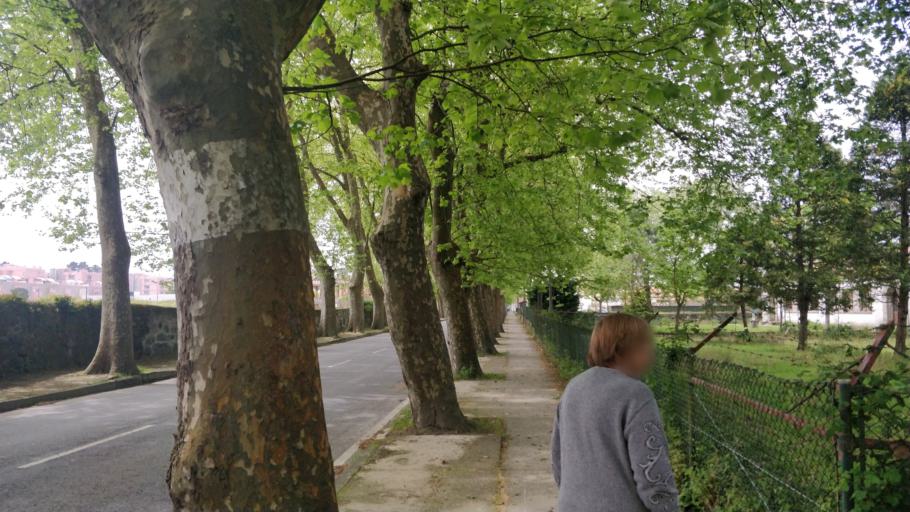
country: PT
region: Viana do Castelo
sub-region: Viana do Castelo
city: Viana do Castelo
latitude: 41.6858
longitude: -8.8168
